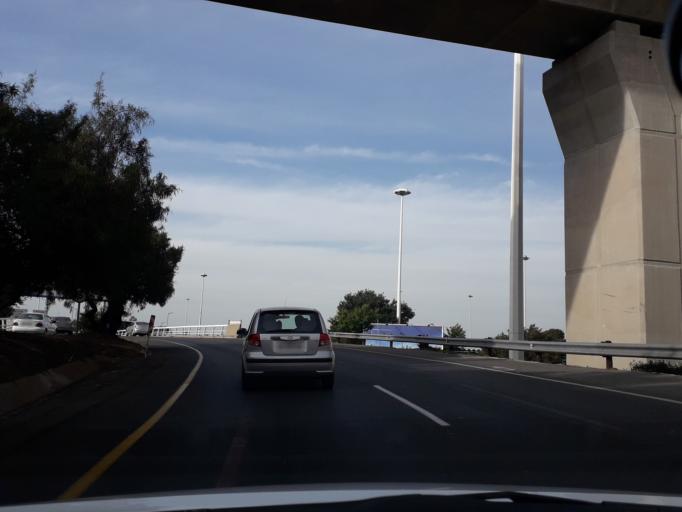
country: ZA
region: Gauteng
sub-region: City of Johannesburg Metropolitan Municipality
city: Modderfontein
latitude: -26.1319
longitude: 28.2290
